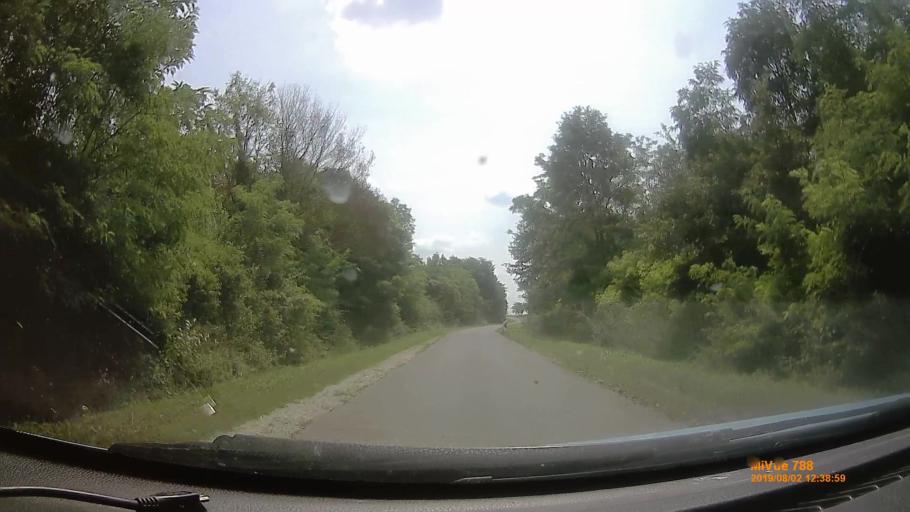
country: HU
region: Baranya
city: Buekkoesd
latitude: 46.0926
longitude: 17.9581
